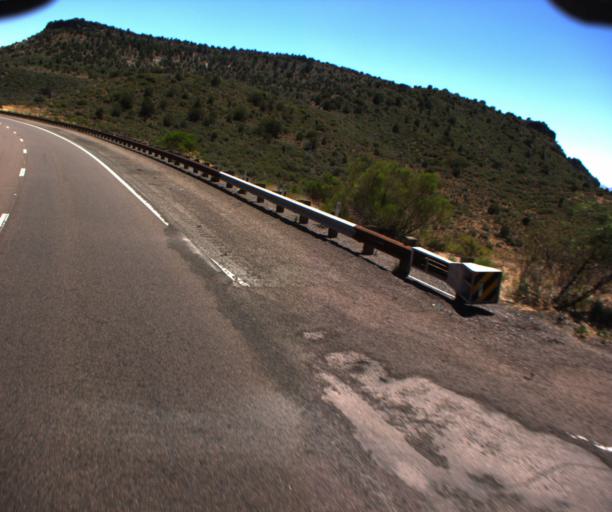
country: US
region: Arizona
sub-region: Gila County
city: Tonto Basin
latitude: 33.9214
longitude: -111.4551
